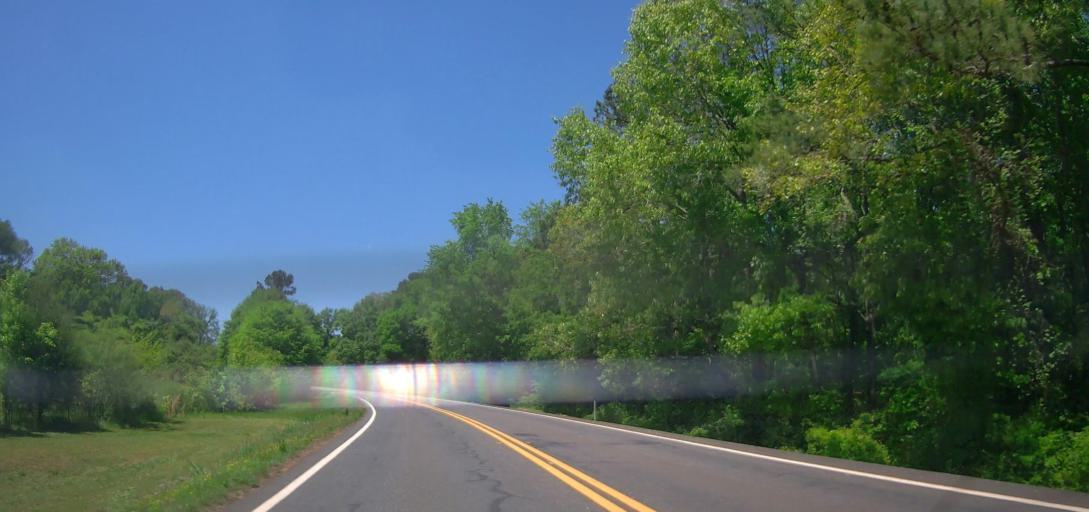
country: US
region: Georgia
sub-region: Jasper County
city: Monticello
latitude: 33.2815
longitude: -83.6196
